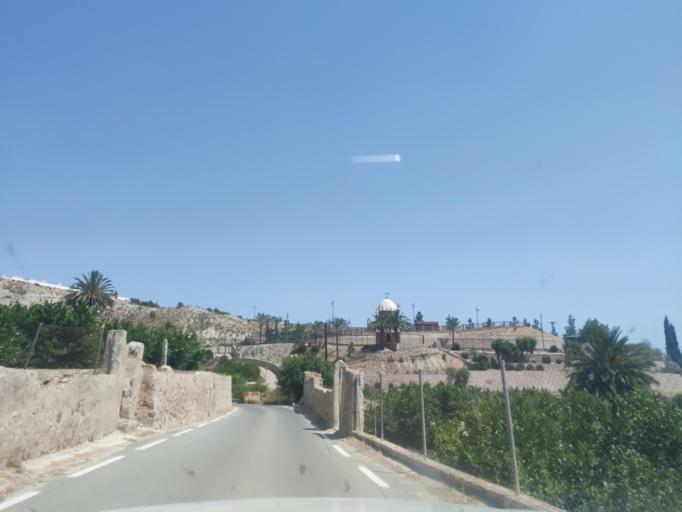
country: ES
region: Murcia
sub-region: Murcia
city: Ulea
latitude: 38.1428
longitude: -1.3217
